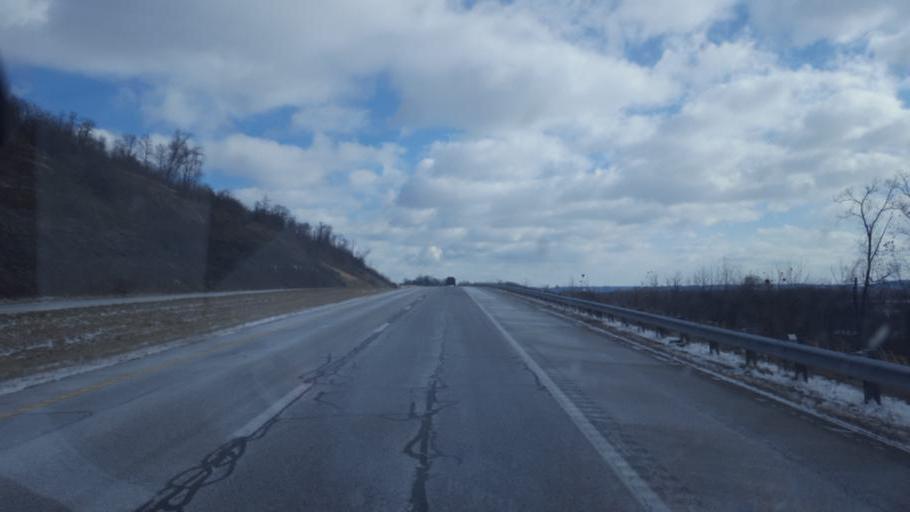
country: US
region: Ohio
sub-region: Muskingum County
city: Dresden
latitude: 40.1510
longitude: -82.0606
